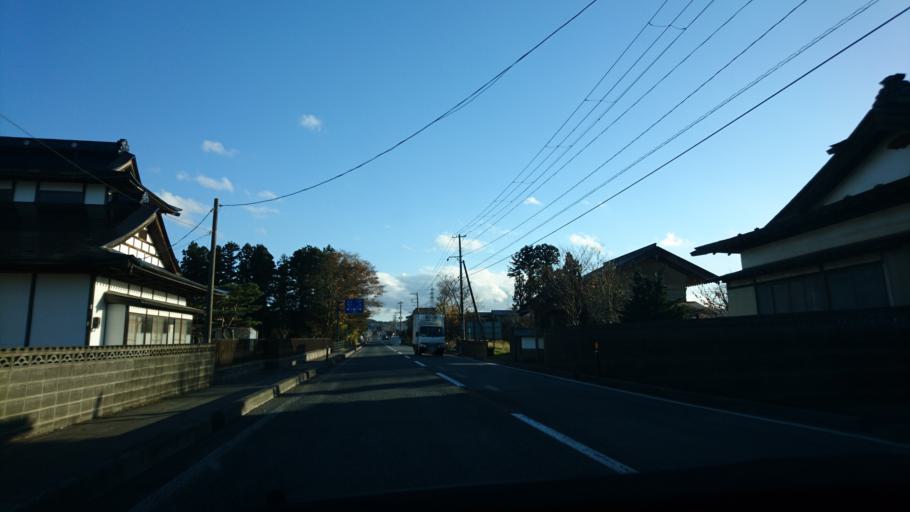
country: JP
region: Iwate
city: Ichinoseki
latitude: 38.9769
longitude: 141.1168
